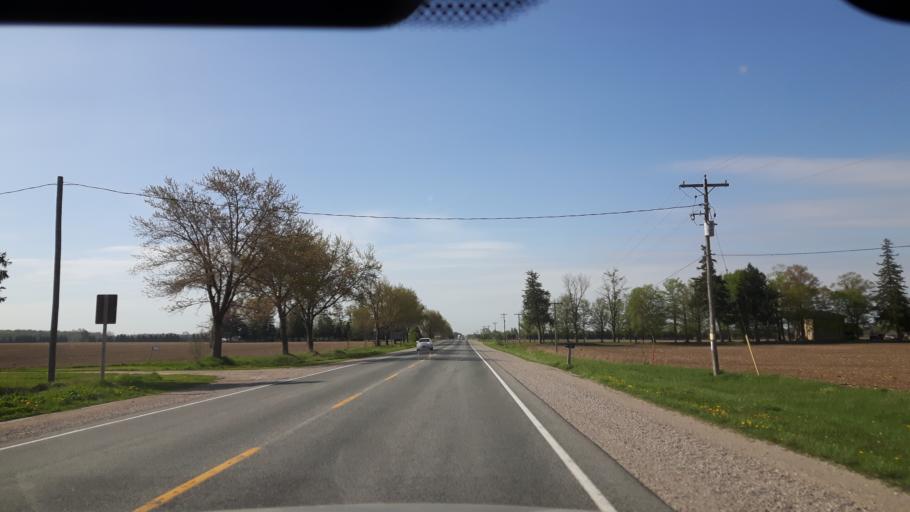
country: CA
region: Ontario
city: Bluewater
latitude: 43.5206
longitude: -81.5163
